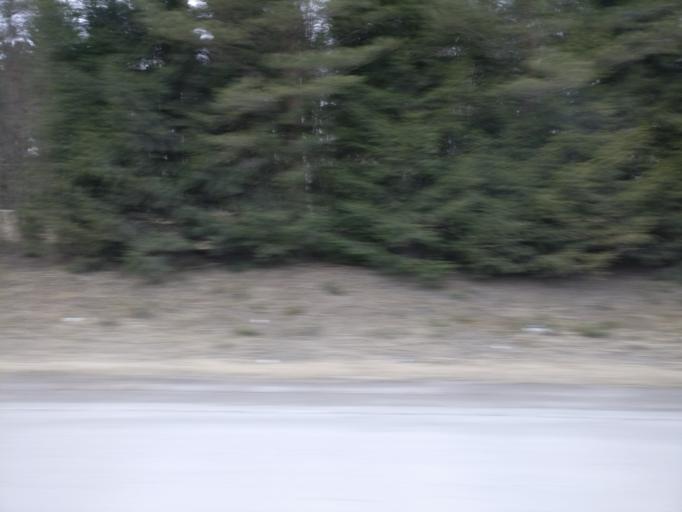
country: FI
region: Uusimaa
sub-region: Helsinki
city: Nurmijaervi
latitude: 60.4996
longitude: 24.8508
